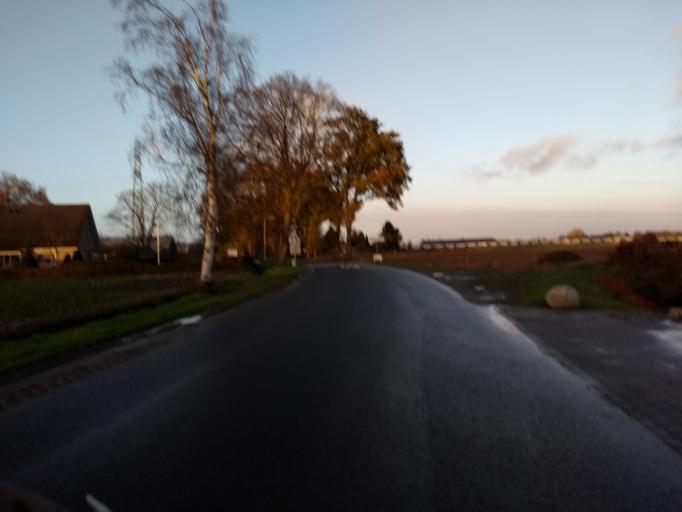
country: NL
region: Overijssel
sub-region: Gemeente Almelo
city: Almelo
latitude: 52.3925
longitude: 6.6899
